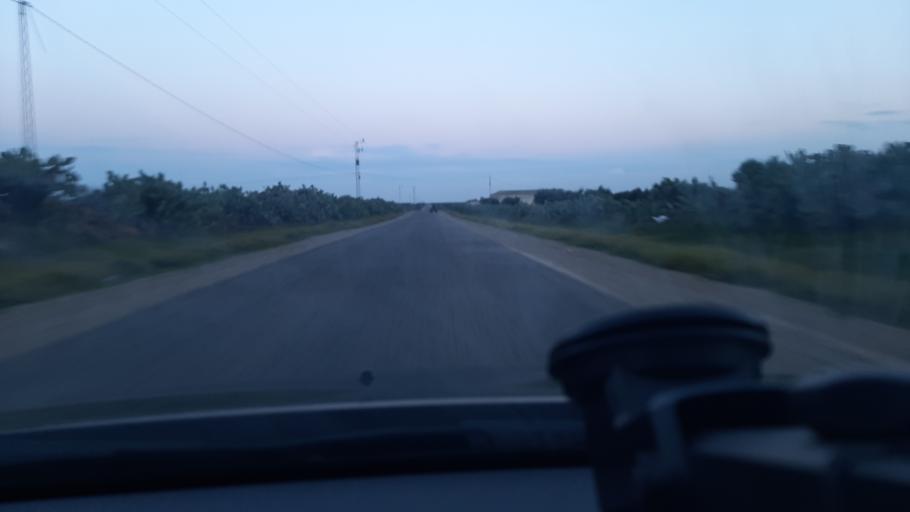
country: TN
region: Al Mahdiyah
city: Shurban
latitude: 35.0157
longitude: 10.4433
